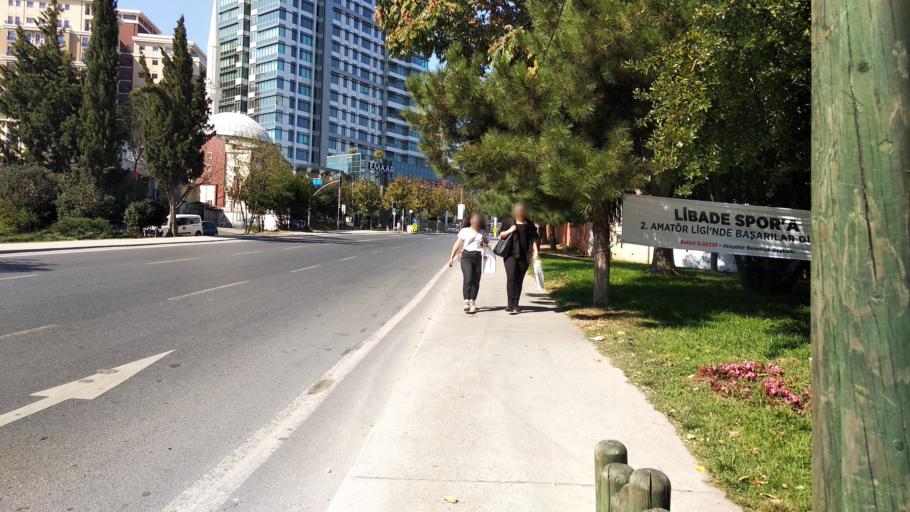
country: TR
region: Istanbul
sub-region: Atasehir
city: Atasehir
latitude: 41.0015
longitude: 29.0732
